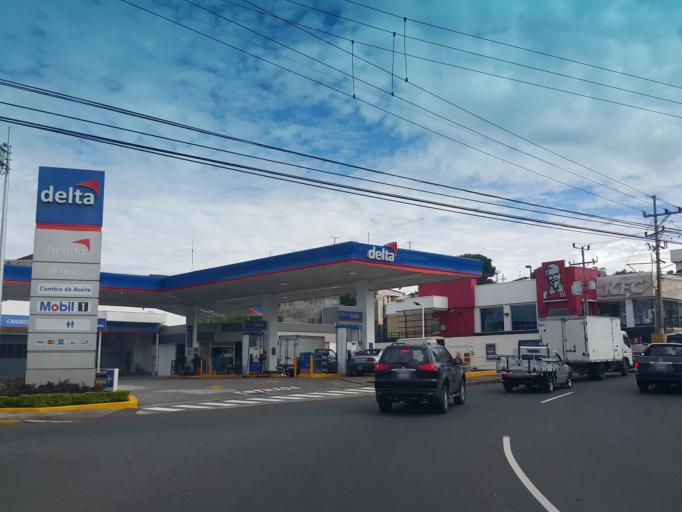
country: CR
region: Heredia
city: Heredia
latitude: 9.9951
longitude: -84.1123
